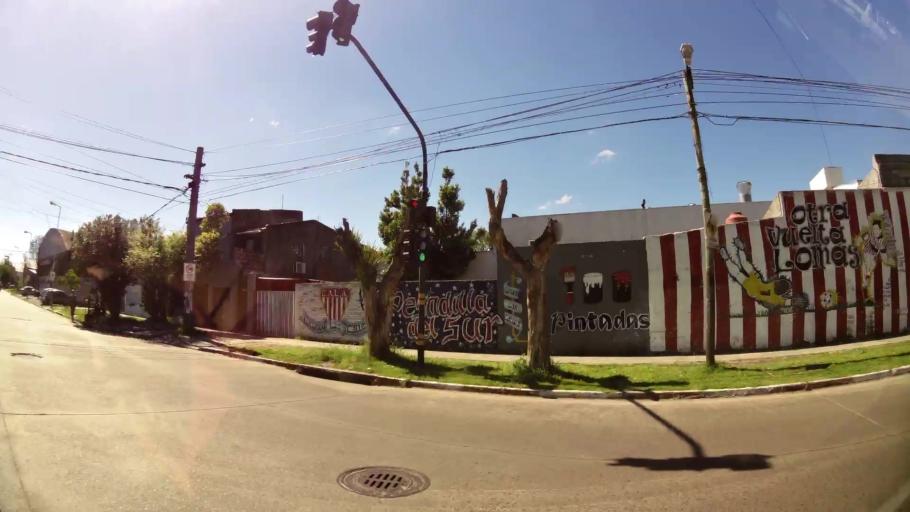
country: AR
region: Buenos Aires
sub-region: Partido de Lomas de Zamora
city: Lomas de Zamora
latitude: -34.7517
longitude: -58.4201
